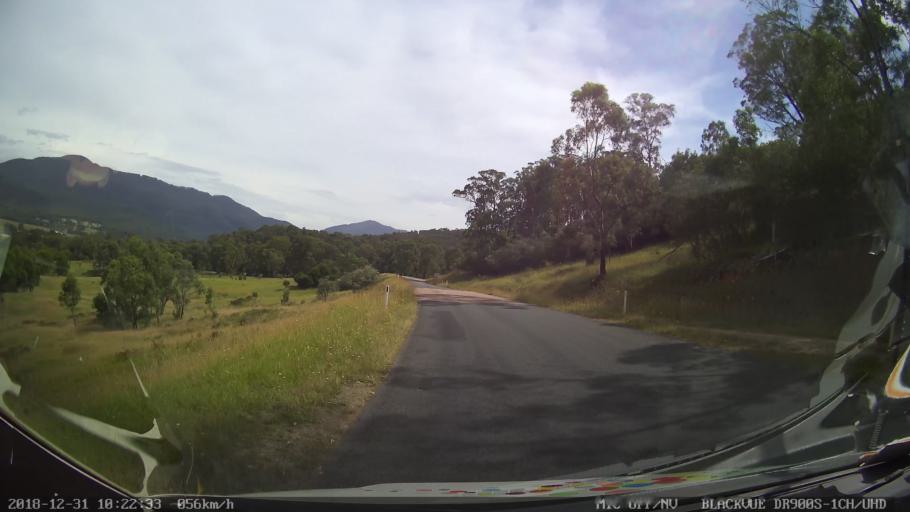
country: AU
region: New South Wales
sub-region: Snowy River
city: Jindabyne
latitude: -36.5245
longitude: 148.1432
